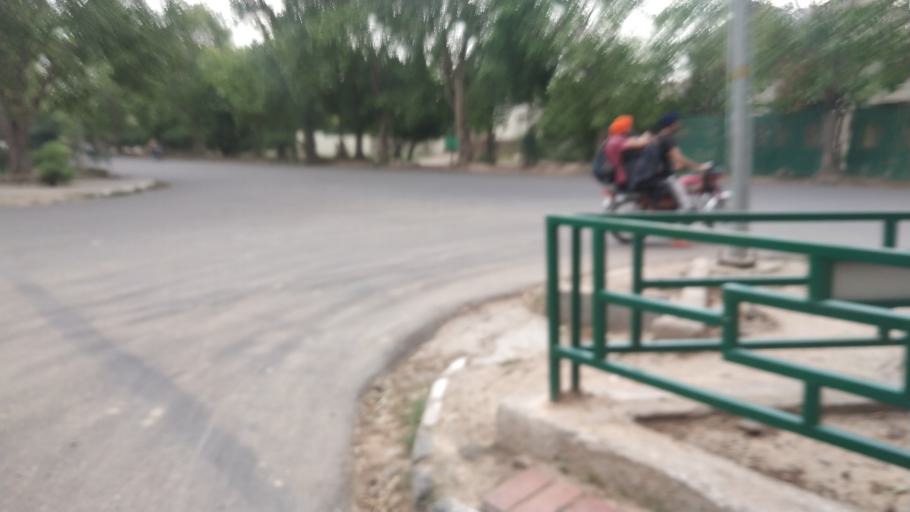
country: IN
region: Punjab
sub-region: Ajitgarh
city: Mohali
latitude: 30.6944
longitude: 76.7171
